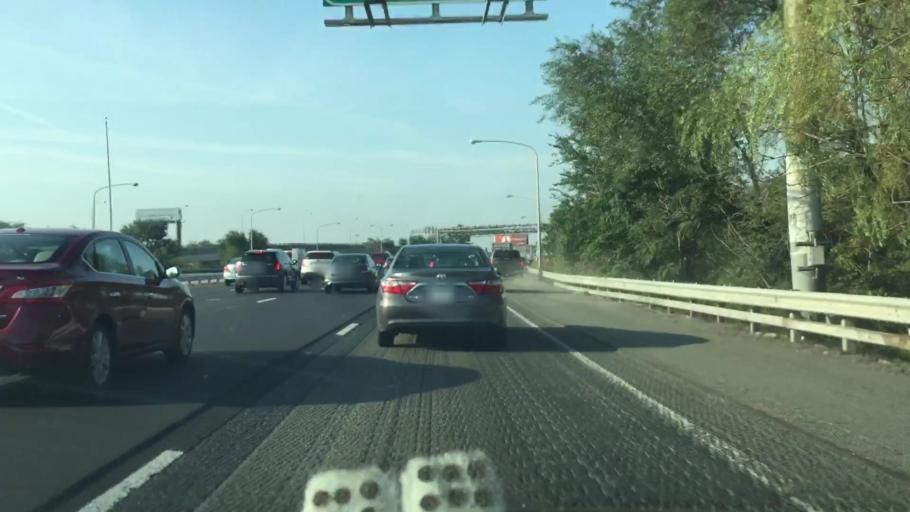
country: US
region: New Jersey
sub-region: Camden County
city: Pennsauken
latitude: 39.9894
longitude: -75.0878
